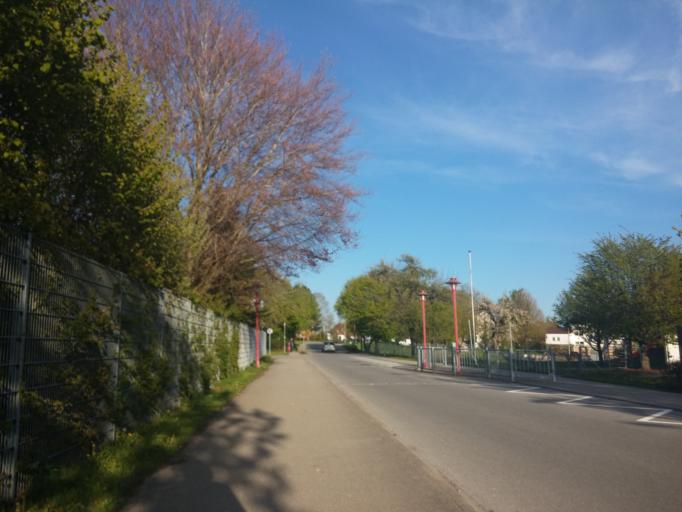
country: DE
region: Baden-Wuerttemberg
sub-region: Tuebingen Region
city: Bad Schussenried
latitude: 48.0047
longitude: 9.6505
